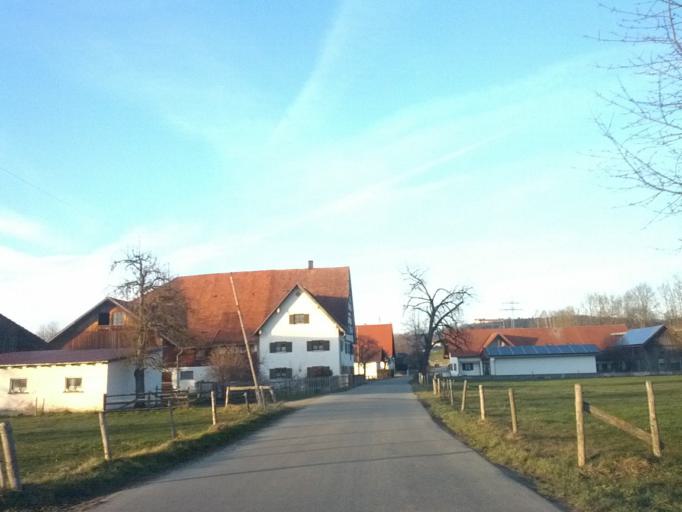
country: DE
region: Bavaria
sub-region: Swabia
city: Kronburg
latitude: 47.8866
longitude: 10.1618
